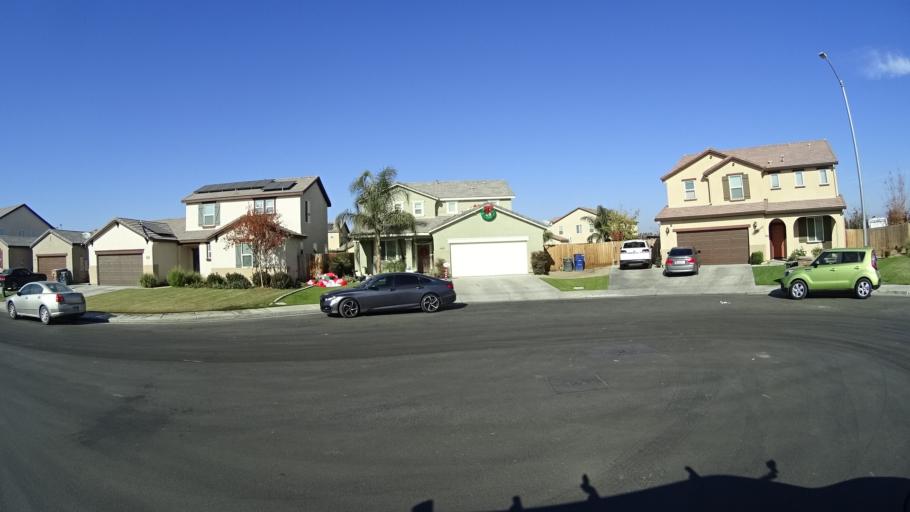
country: US
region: California
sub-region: Kern County
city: Greenfield
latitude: 35.2901
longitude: -119.0592
